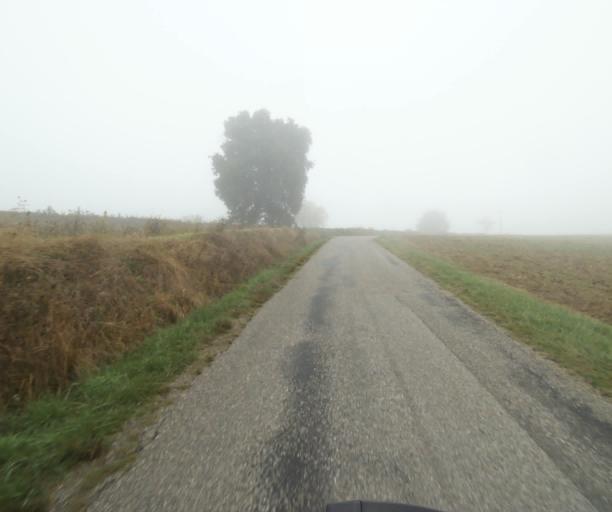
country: FR
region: Midi-Pyrenees
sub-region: Departement de la Haute-Garonne
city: Villemur-sur-Tarn
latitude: 43.8994
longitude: 1.4865
